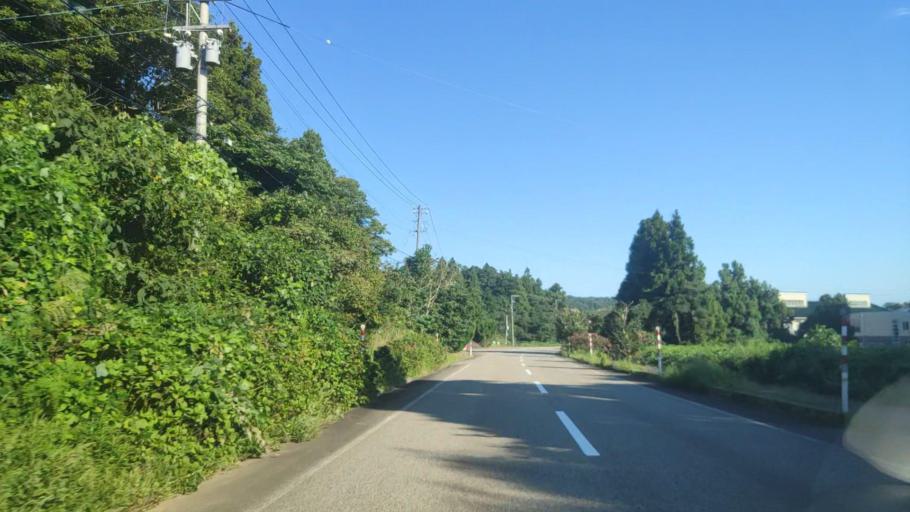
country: JP
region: Ishikawa
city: Nanao
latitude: 37.1251
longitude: 136.9273
